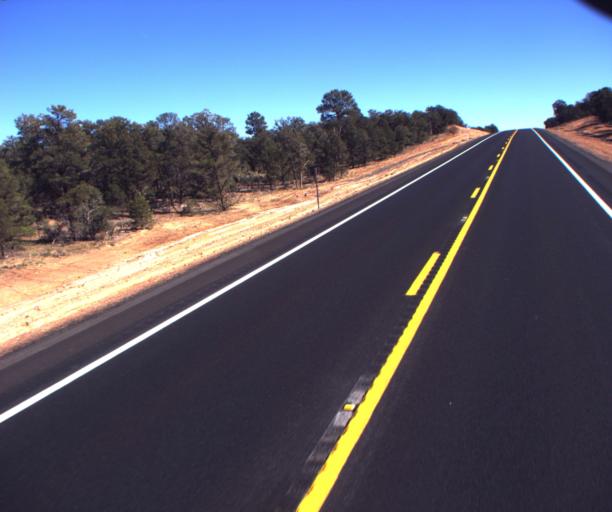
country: US
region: Arizona
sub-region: Apache County
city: Ganado
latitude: 35.7148
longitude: -109.3384
